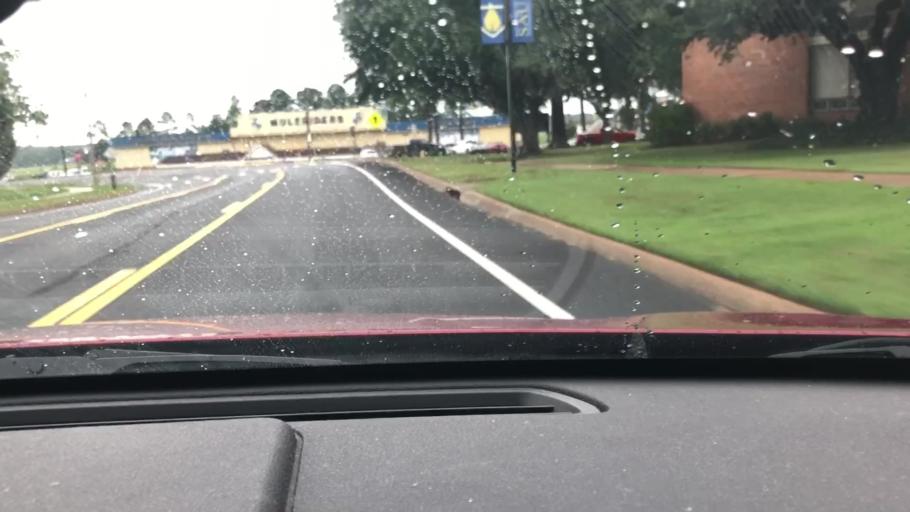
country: US
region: Arkansas
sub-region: Columbia County
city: Magnolia
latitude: 33.2932
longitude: -93.2370
